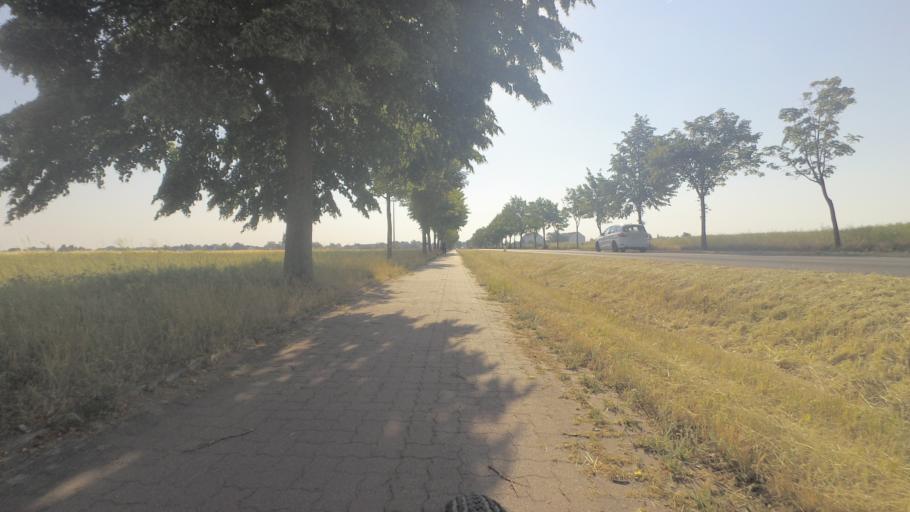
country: DE
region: Saxony-Anhalt
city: Osternienburger Land
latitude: 51.7908
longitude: 12.0160
